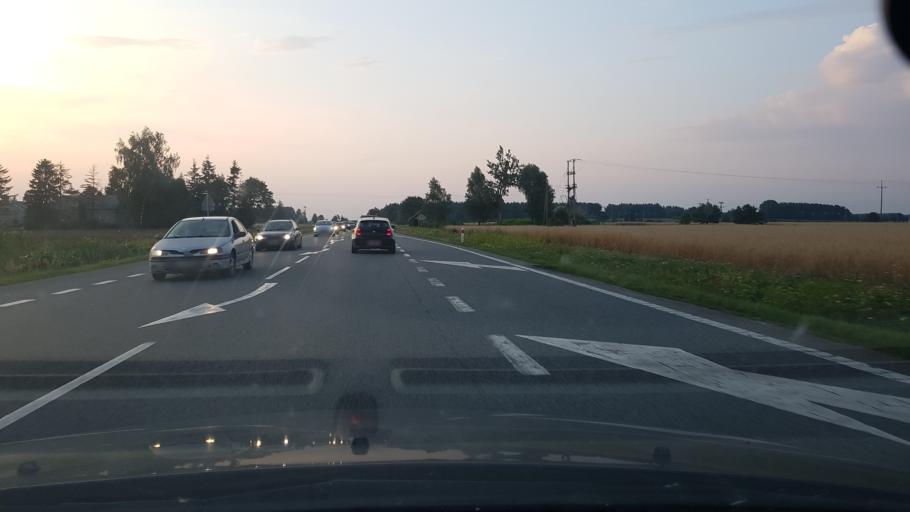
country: PL
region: Masovian Voivodeship
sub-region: Powiat mlawski
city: Wieczfnia Koscielna
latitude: 53.2016
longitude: 20.4353
